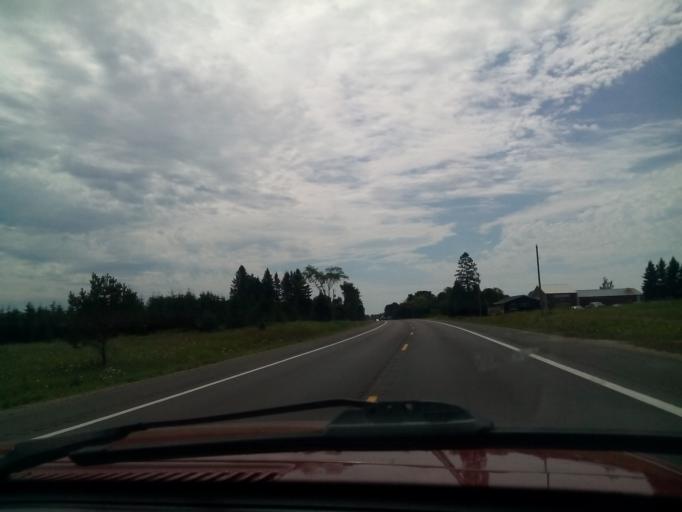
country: US
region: Michigan
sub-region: Schoolcraft County
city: Manistique
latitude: 46.0790
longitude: -85.9582
